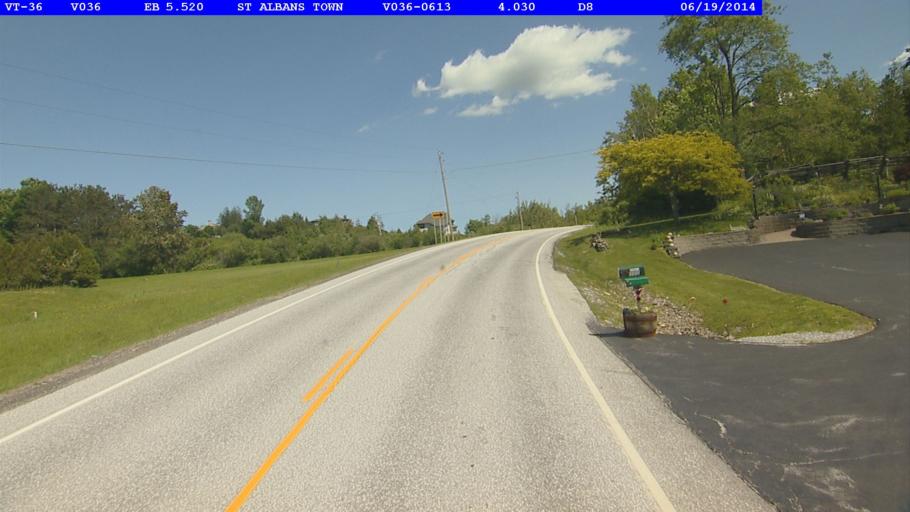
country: US
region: Vermont
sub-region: Franklin County
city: Saint Albans
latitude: 44.7975
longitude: -73.0525
